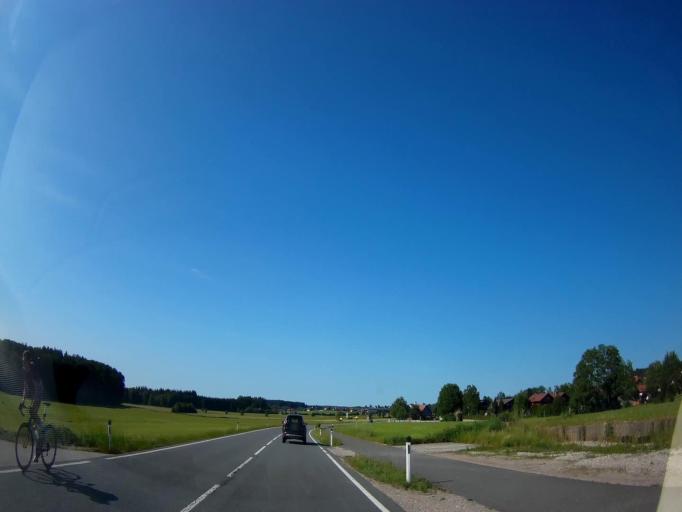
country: AT
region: Salzburg
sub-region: Politischer Bezirk Salzburg-Umgebung
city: Lamprechtshausen
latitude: 47.9745
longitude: 12.9506
